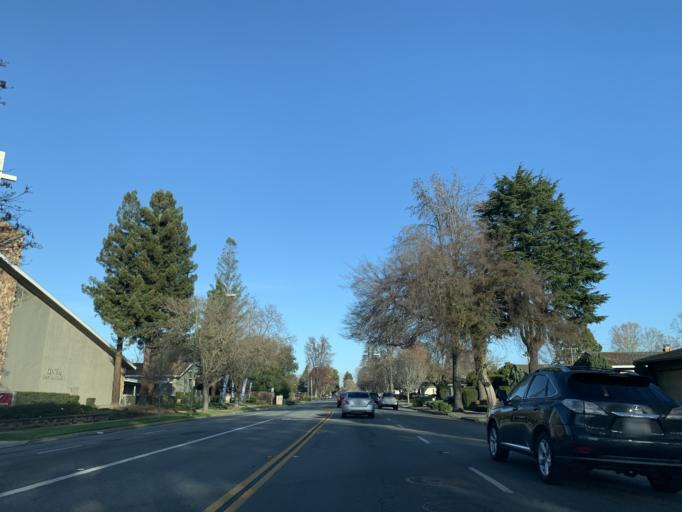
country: US
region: California
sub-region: Santa Clara County
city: Cambrian Park
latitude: 37.2772
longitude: -121.9101
